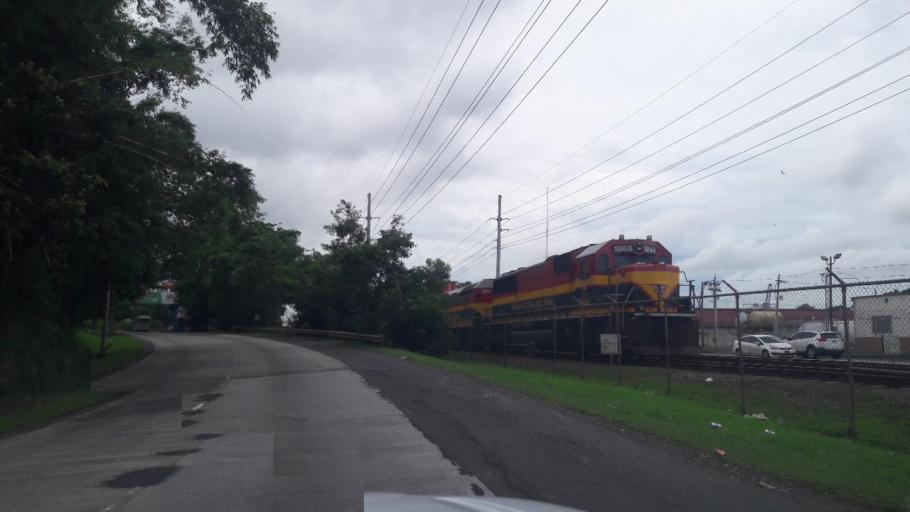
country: PA
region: Panama
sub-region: Distrito de Panama
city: Ancon
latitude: 8.9801
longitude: -79.5703
